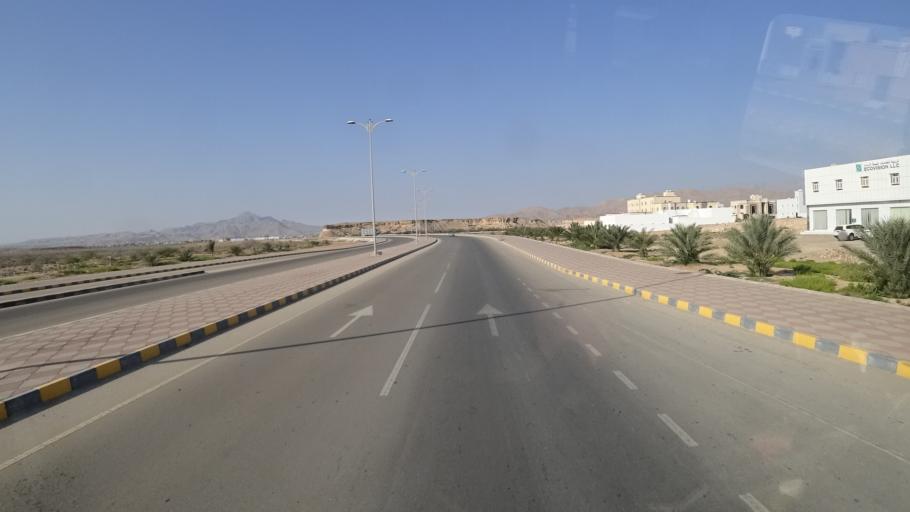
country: OM
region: Ash Sharqiyah
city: Sur
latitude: 22.5998
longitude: 59.4811
